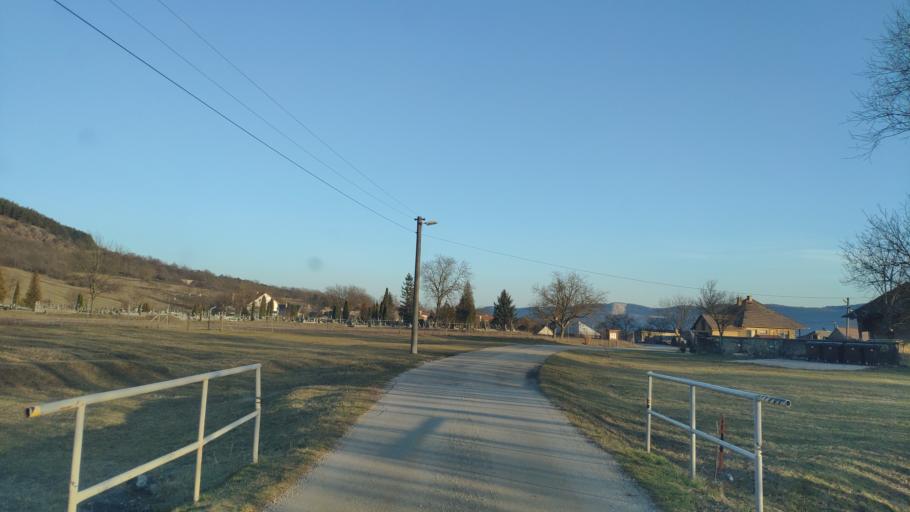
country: SK
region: Kosicky
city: Medzev
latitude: 48.6087
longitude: 20.7489
